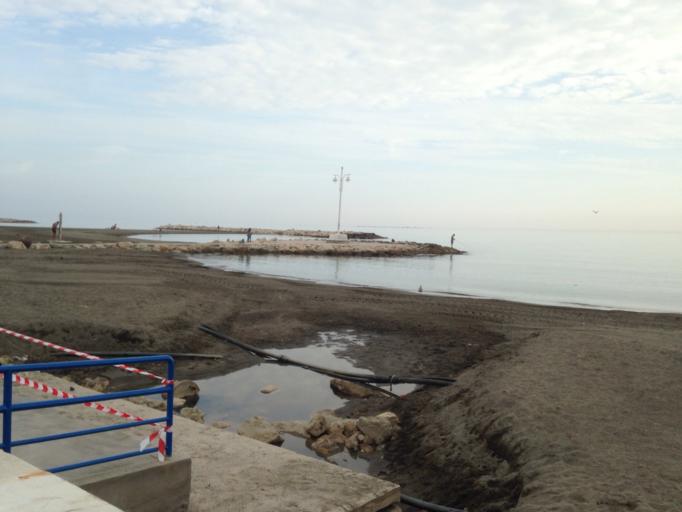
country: ES
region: Andalusia
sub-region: Provincia de Malaga
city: Malaga
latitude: 36.7209
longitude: -4.3749
